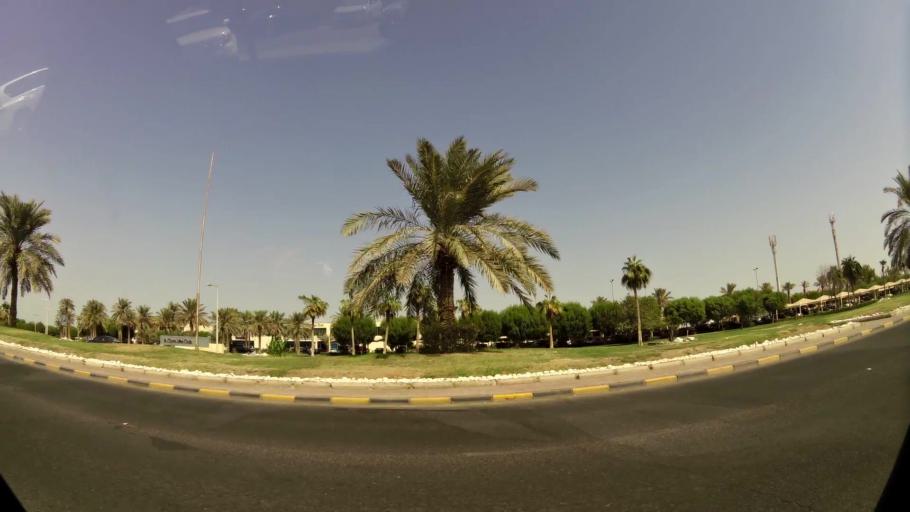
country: KW
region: Muhafazat Hawalli
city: Hawalli
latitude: 29.3427
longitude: 48.0470
